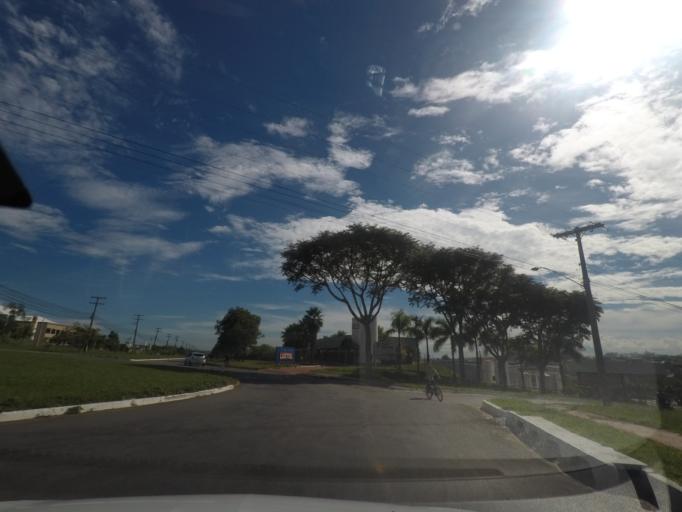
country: BR
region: Goias
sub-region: Aparecida De Goiania
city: Aparecida de Goiania
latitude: -16.7985
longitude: -49.2556
